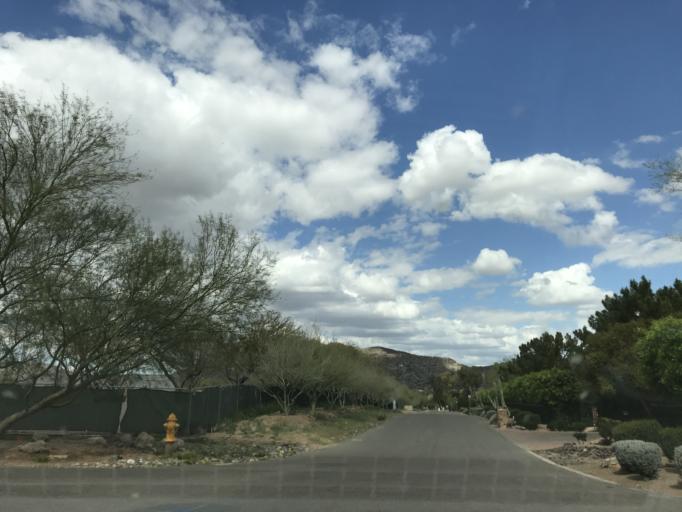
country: US
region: Arizona
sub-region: Maricopa County
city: Paradise Valley
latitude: 33.5211
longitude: -111.9534
